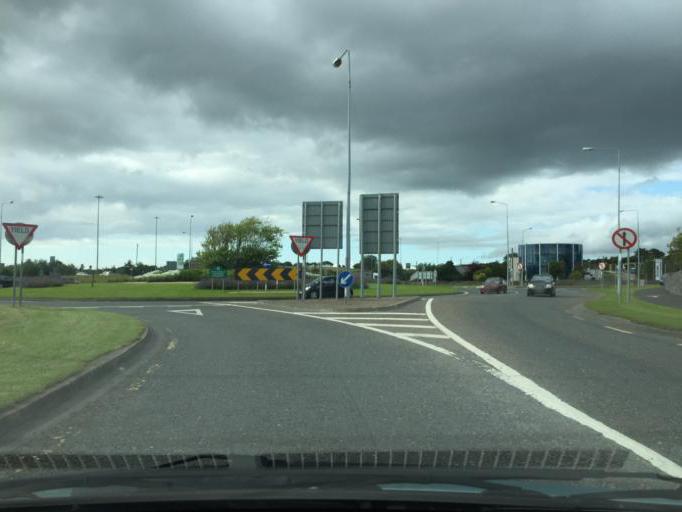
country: IE
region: Connaught
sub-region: Sligo
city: Sligo
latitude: 54.2440
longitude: -8.4762
